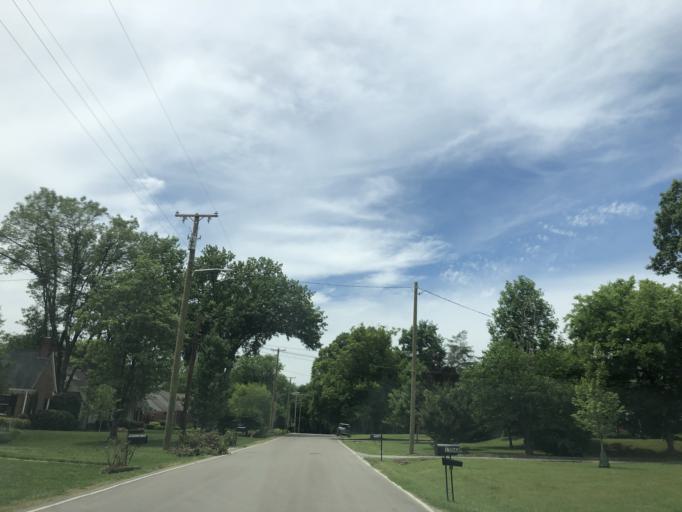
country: US
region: Tennessee
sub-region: Davidson County
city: Oak Hill
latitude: 36.1116
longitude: -86.7978
